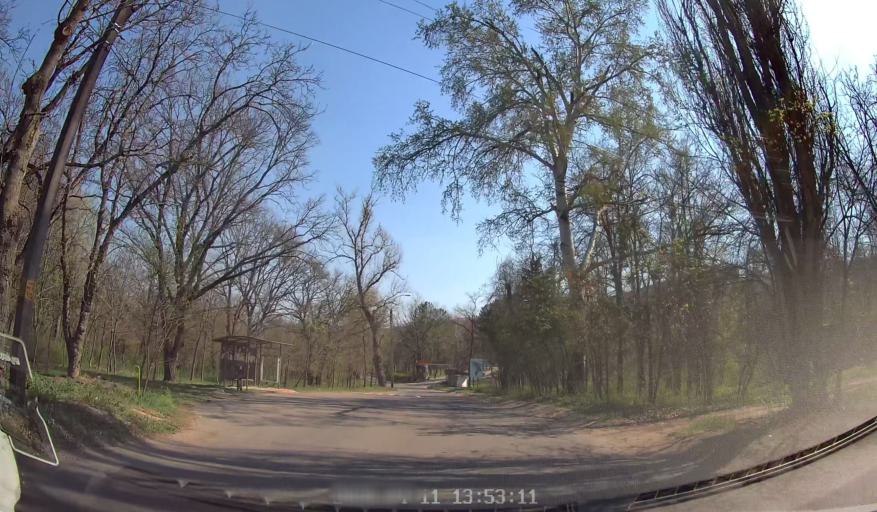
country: MD
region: Chisinau
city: Vadul lui Voda
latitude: 47.0799
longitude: 29.0929
